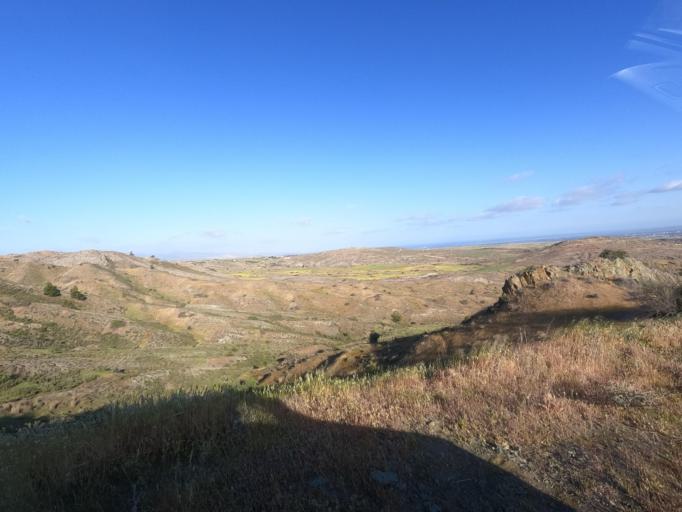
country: CY
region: Lefkosia
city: Peristerona
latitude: 35.0733
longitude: 33.0407
